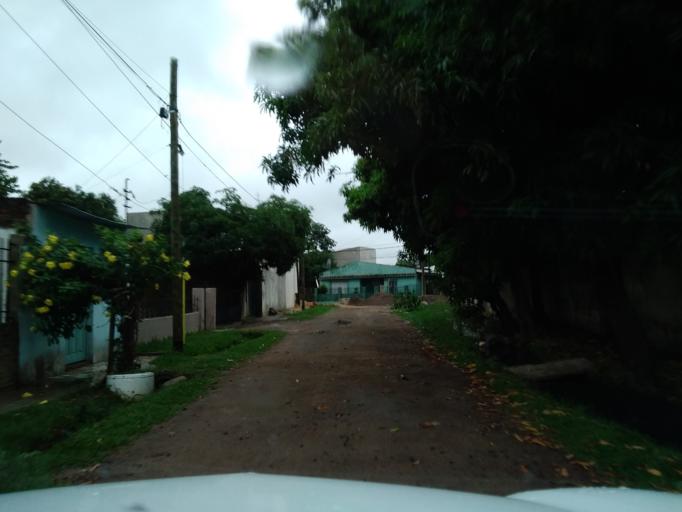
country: AR
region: Corrientes
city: Corrientes
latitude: -27.4952
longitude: -58.8223
